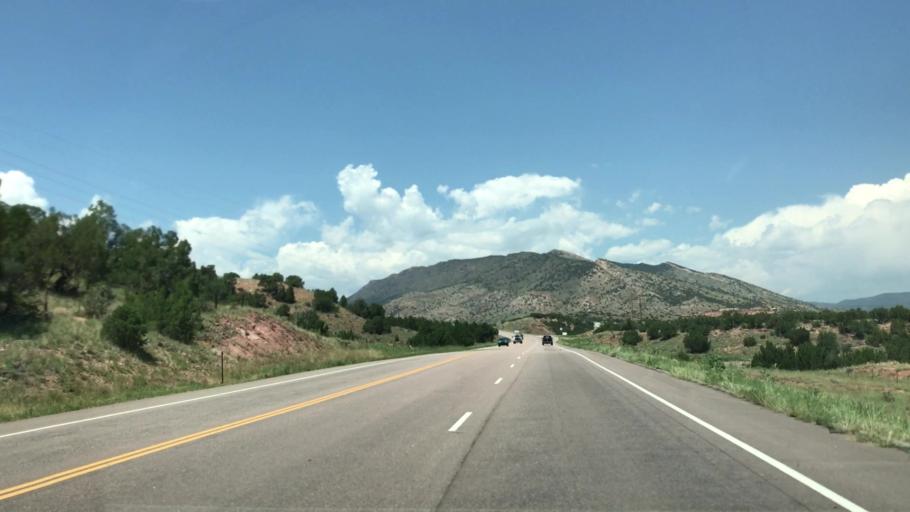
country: US
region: Colorado
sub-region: Fremont County
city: Canon City
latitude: 38.4776
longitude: -105.2618
